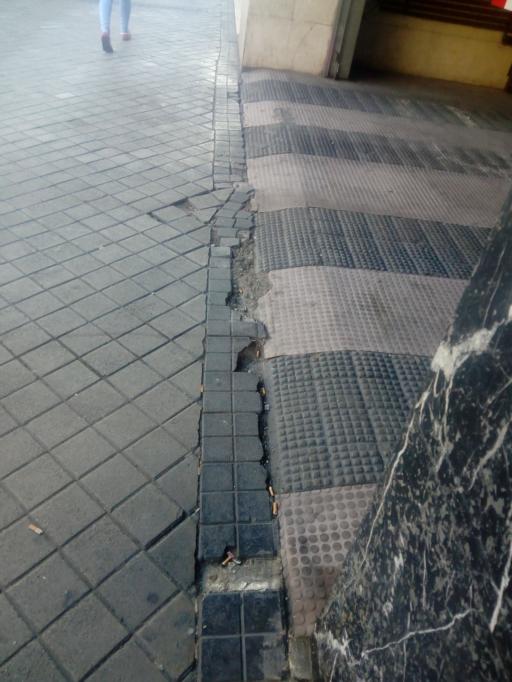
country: ES
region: Madrid
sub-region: Provincia de Madrid
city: Retiro
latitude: 40.4054
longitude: -3.6713
